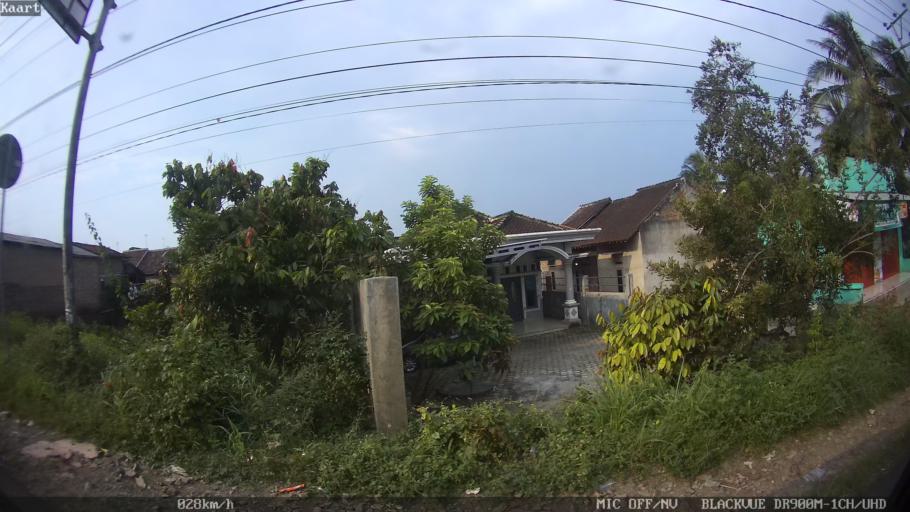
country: ID
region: Lampung
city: Natar
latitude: -5.3657
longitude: 105.1670
